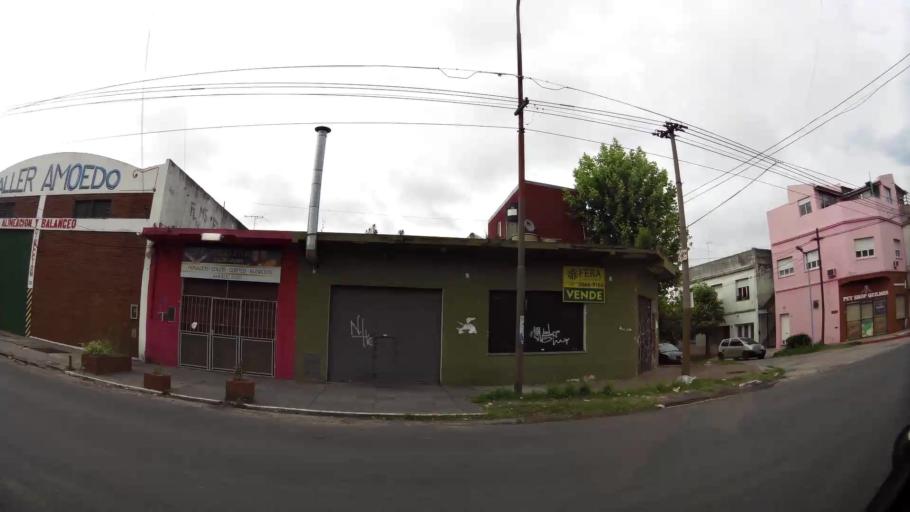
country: AR
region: Buenos Aires
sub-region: Partido de Quilmes
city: Quilmes
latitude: -34.7425
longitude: -58.2802
